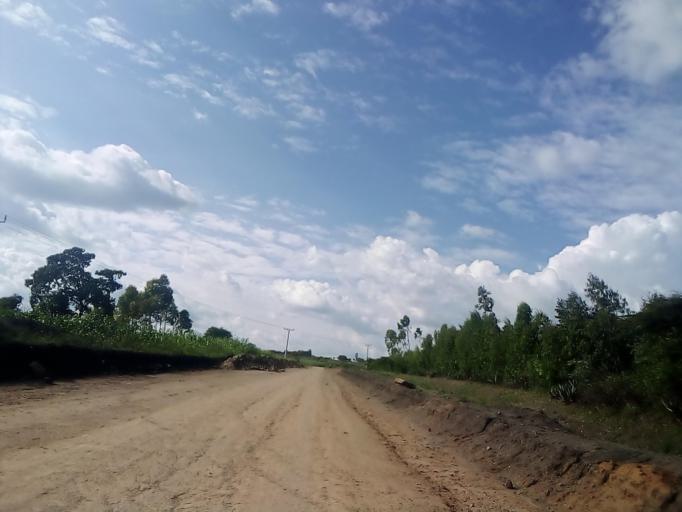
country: ET
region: Southern Nations, Nationalities, and People's Region
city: K'olito
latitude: 7.6250
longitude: 38.0642
